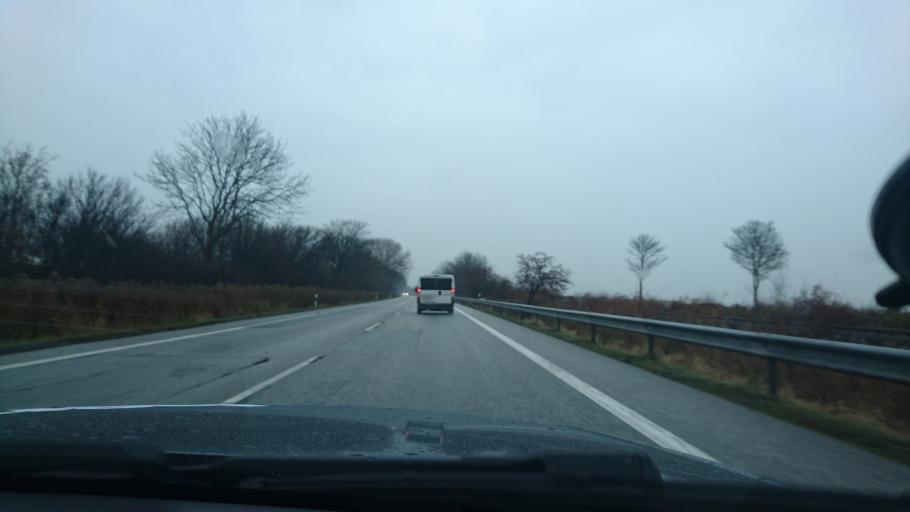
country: DE
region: Schleswig-Holstein
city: Fehmarn
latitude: 54.4406
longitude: 11.1606
